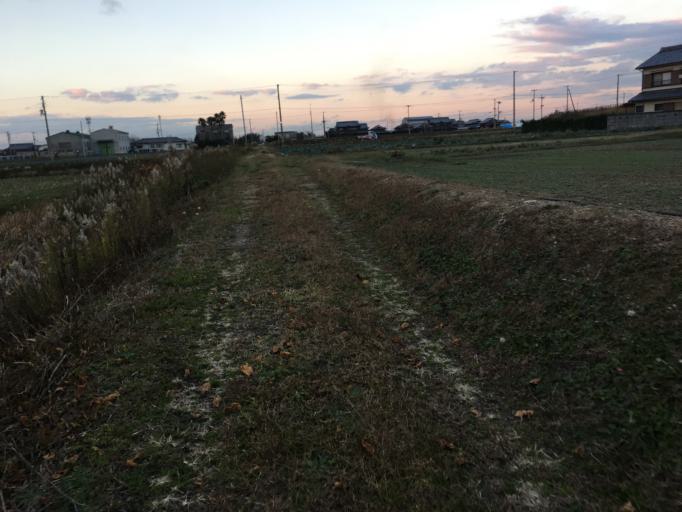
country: JP
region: Hyogo
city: Miki
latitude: 34.7355
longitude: 134.9506
